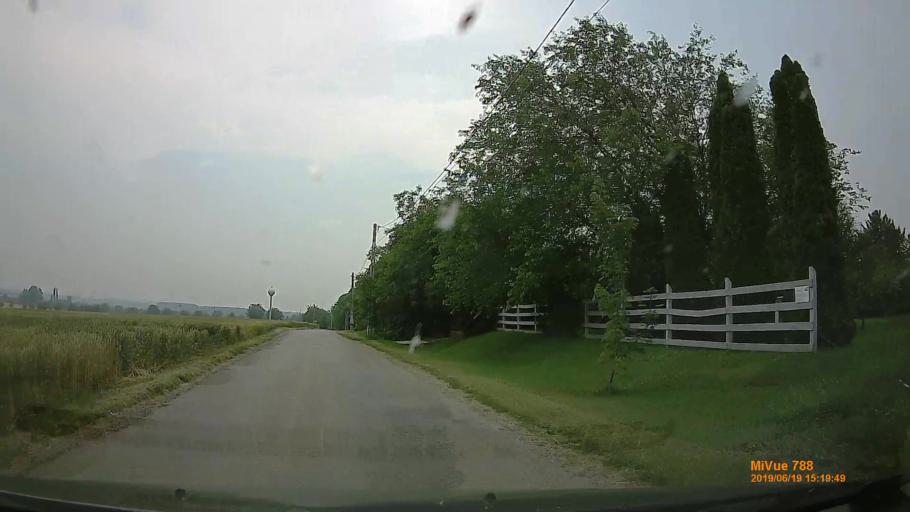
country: HU
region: Baranya
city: Szigetvar
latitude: 46.0706
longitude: 17.8503
